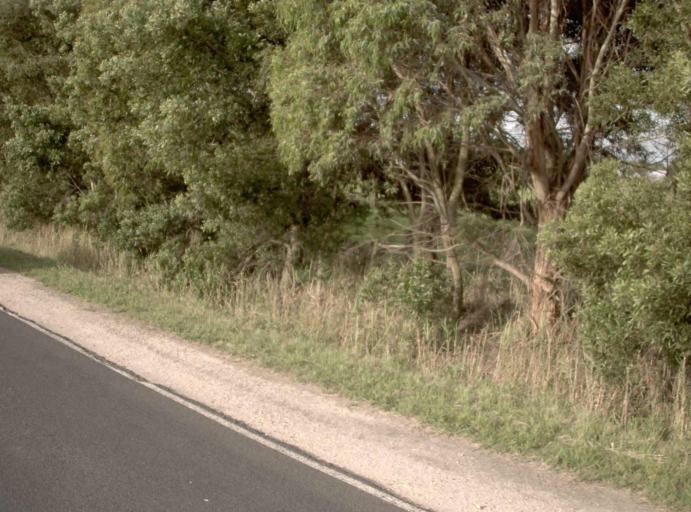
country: AU
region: Victoria
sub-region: Wellington
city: Sale
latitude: -37.9112
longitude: 146.9962
